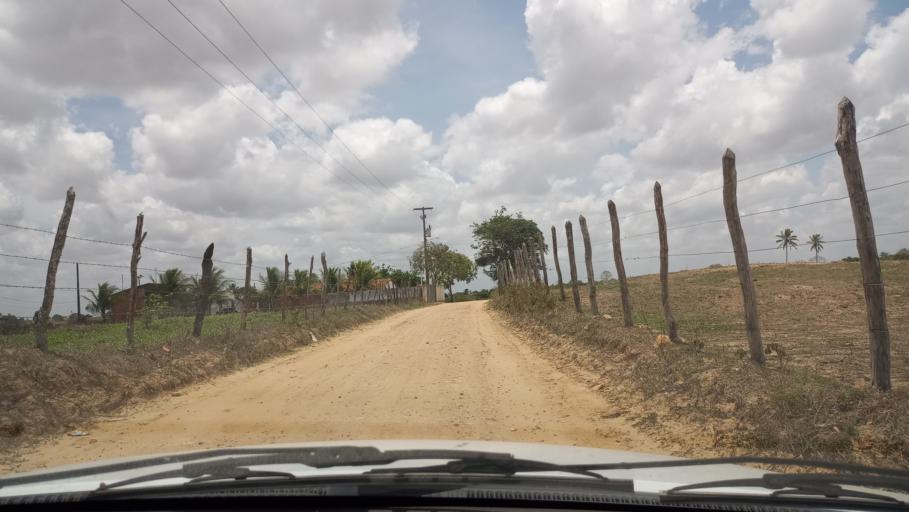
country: BR
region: Rio Grande do Norte
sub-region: Brejinho
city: Brejinho
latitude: -6.2746
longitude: -35.3330
